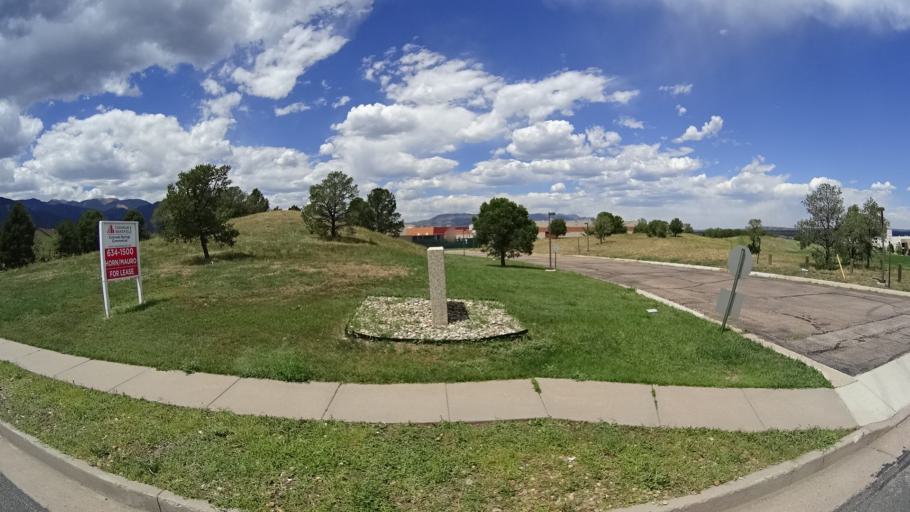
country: US
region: Colorado
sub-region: El Paso County
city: Stratmoor
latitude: 38.7811
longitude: -104.8027
